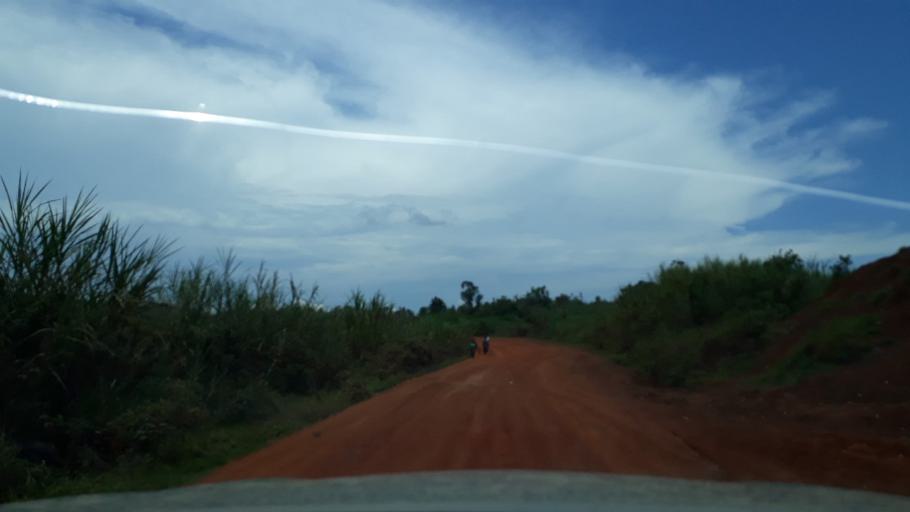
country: CD
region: Eastern Province
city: Bunia
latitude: 1.7145
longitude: 30.2942
